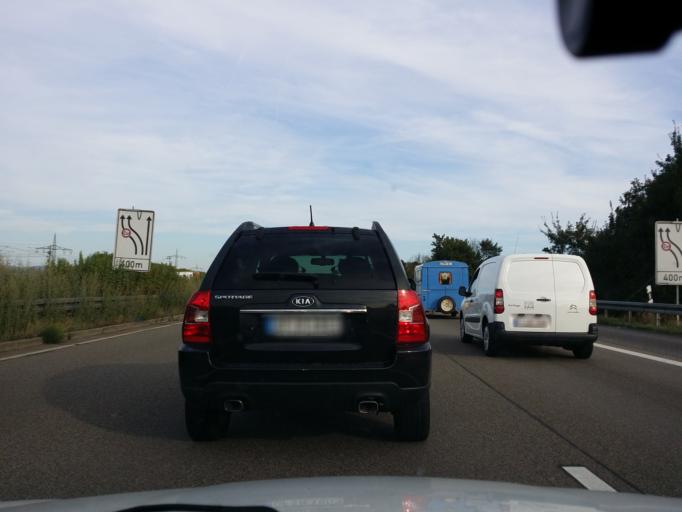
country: DE
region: Hesse
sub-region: Regierungsbezirk Giessen
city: Runkel
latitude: 50.3614
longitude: 8.1333
